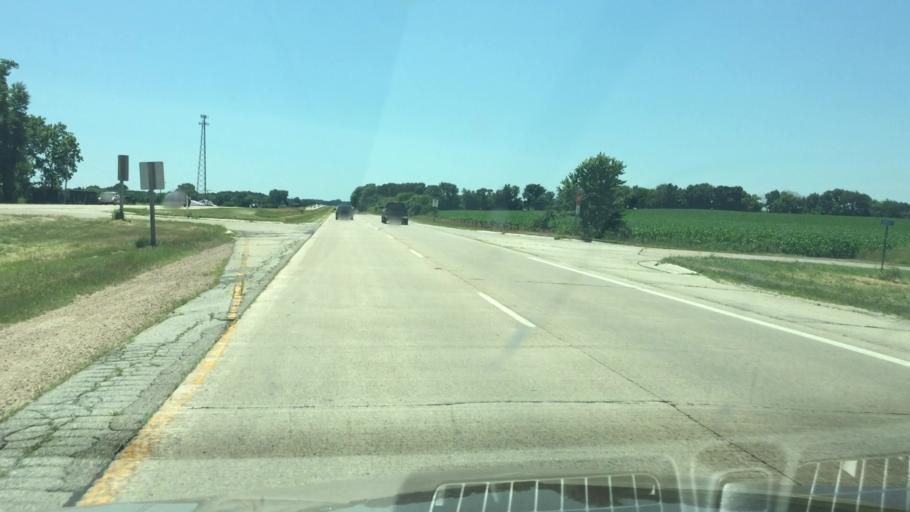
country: US
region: Wisconsin
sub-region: Dodge County
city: Beaver Dam
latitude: 43.4083
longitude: -88.9188
